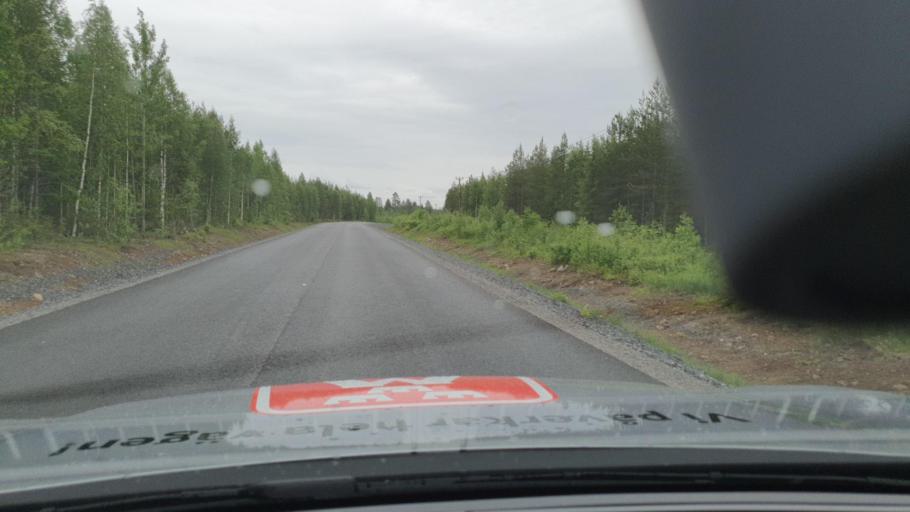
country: SE
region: Norrbotten
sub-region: Overkalix Kommun
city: OEverkalix
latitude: 66.7219
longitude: 23.1855
